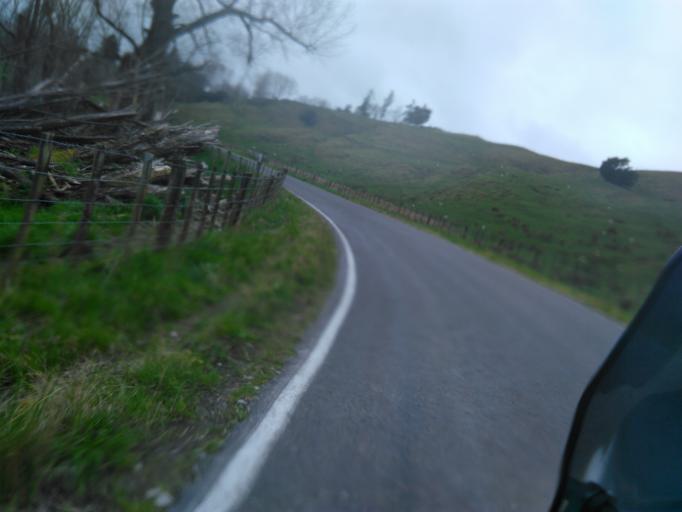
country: NZ
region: Gisborne
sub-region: Gisborne District
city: Gisborne
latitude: -38.6398
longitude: 177.6879
